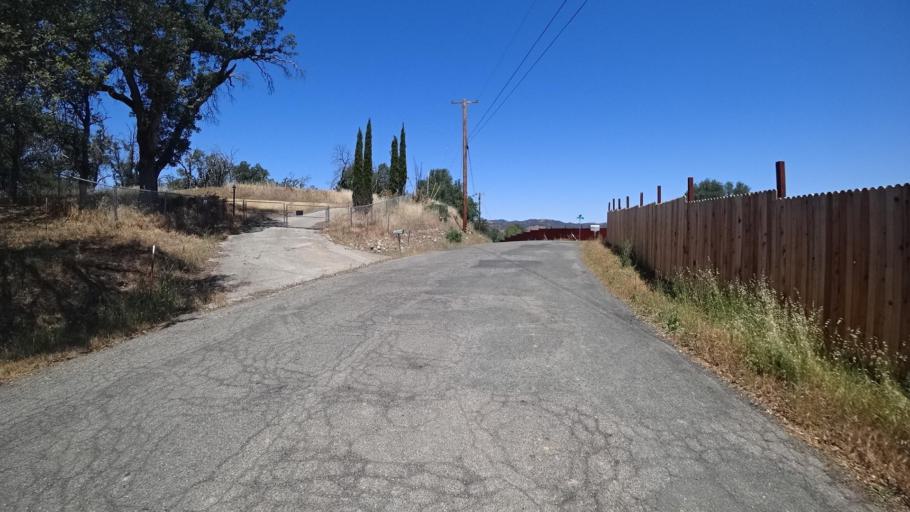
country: US
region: California
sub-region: Lake County
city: Lower Lake
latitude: 38.9123
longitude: -122.5943
